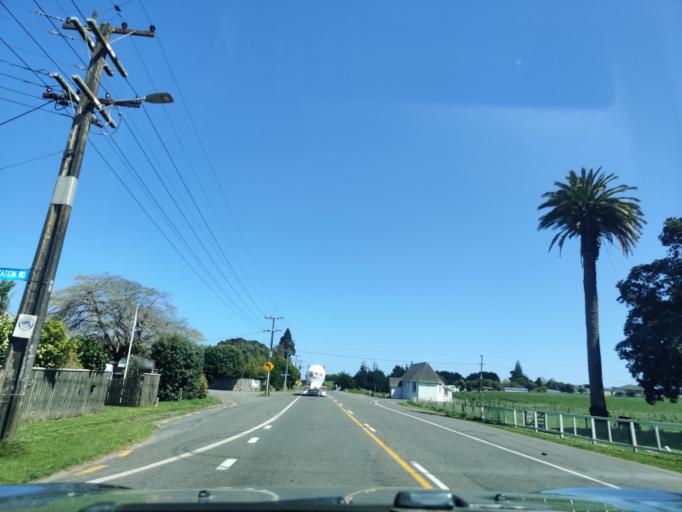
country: NZ
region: Manawatu-Wanganui
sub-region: Wanganui District
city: Wanganui
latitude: -39.8211
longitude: 174.8631
